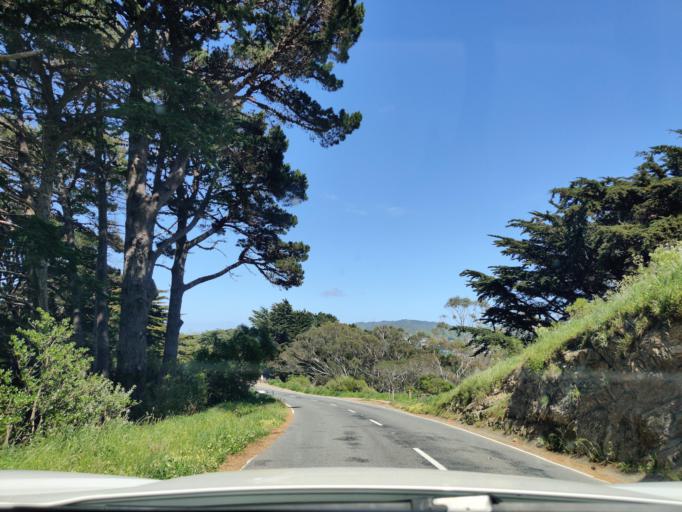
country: NZ
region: Wellington
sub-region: Wellington City
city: Wellington
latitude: -41.2993
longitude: 174.7919
